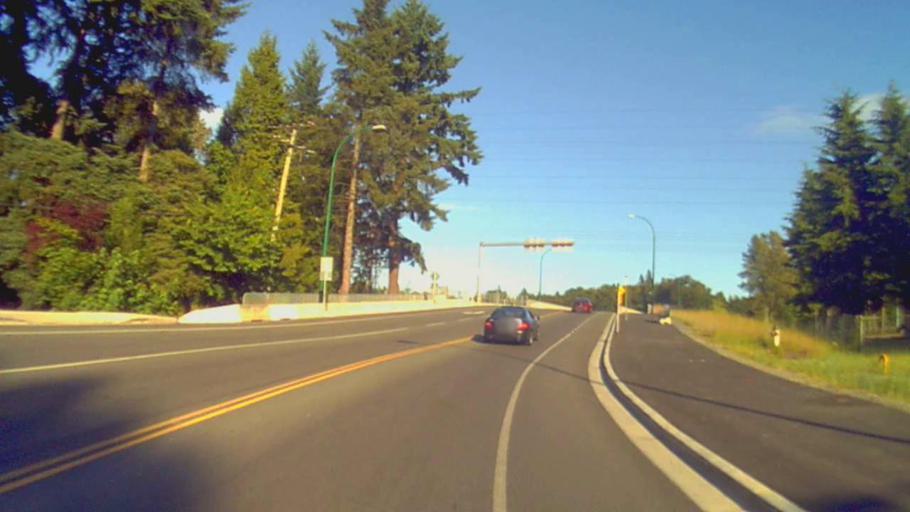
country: CA
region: British Columbia
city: New Westminster
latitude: 49.2454
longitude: -122.9109
